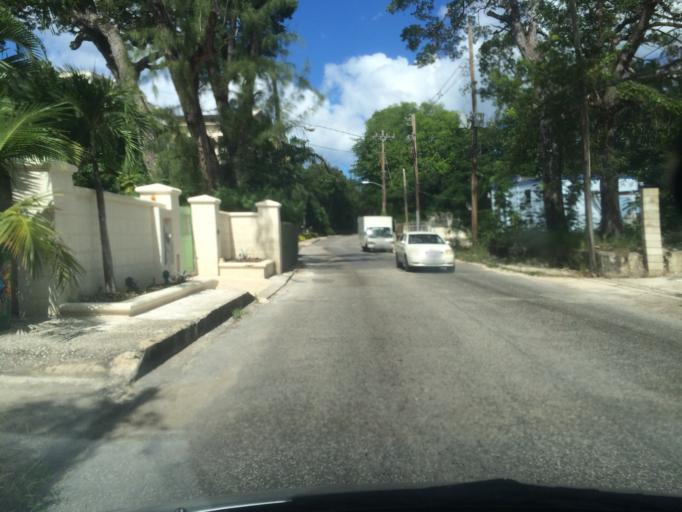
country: BB
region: Saint James
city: Holetown
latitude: 13.1675
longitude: -59.6367
